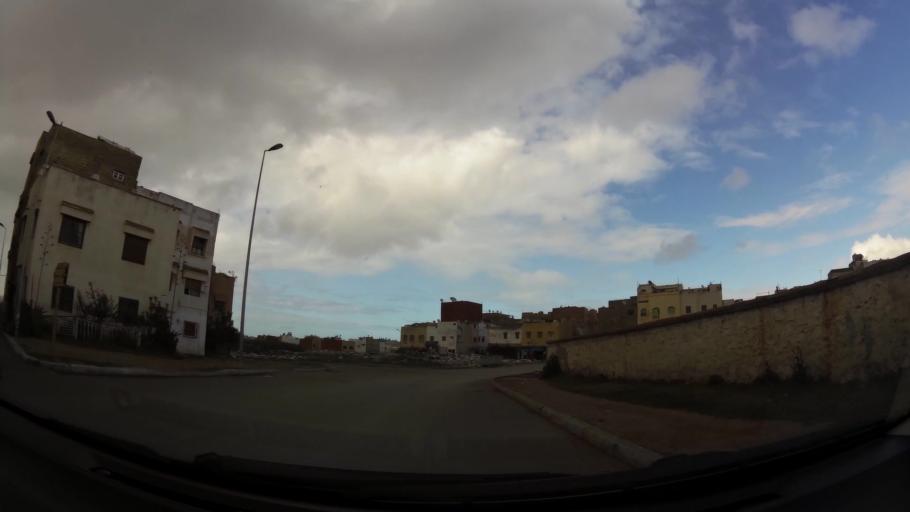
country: MA
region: Grand Casablanca
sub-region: Casablanca
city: Casablanca
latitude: 33.5610
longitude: -7.6964
